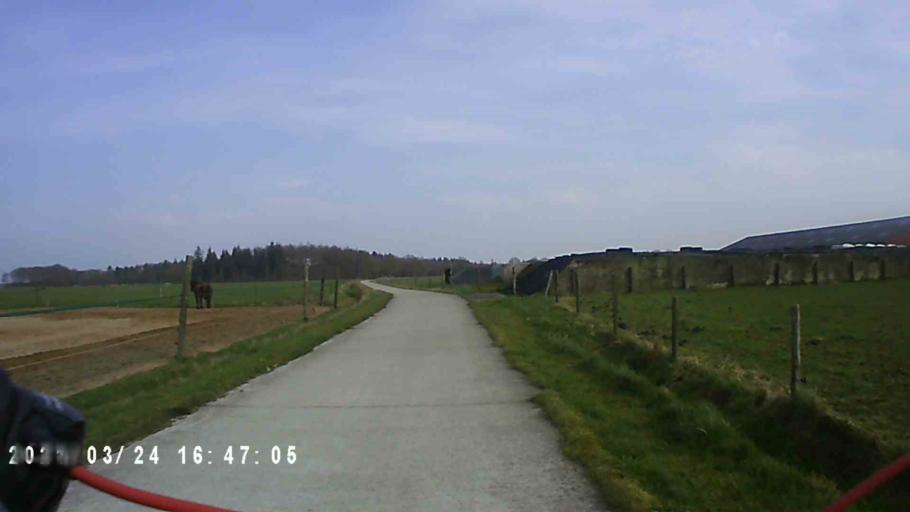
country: NL
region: Groningen
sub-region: Gemeente Leek
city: Leek
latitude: 53.0471
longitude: 6.2801
